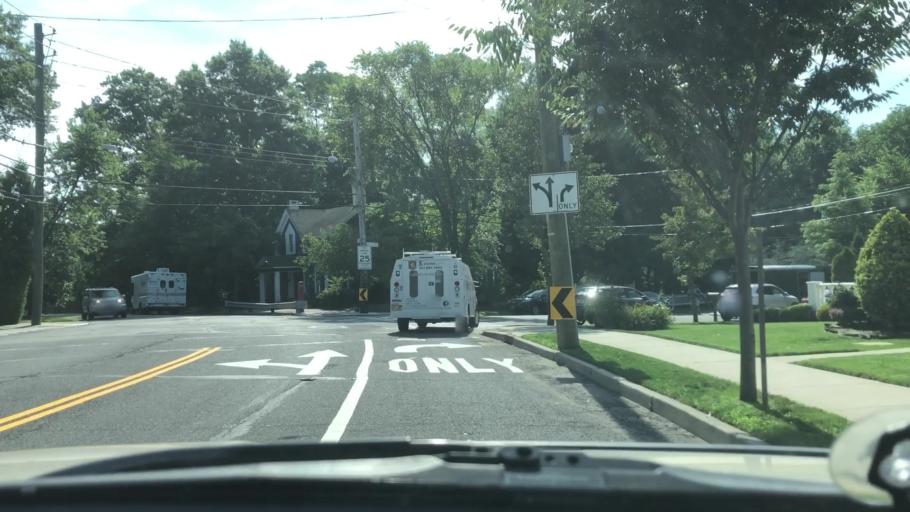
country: US
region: New York
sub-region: Richmond County
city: Staten Island
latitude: 40.5355
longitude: -74.1792
